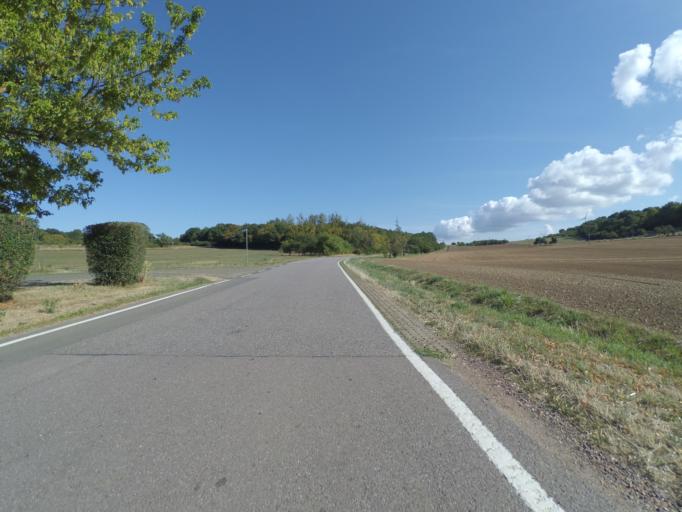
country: DE
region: Saarland
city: Perl
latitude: 49.5069
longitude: 6.4082
